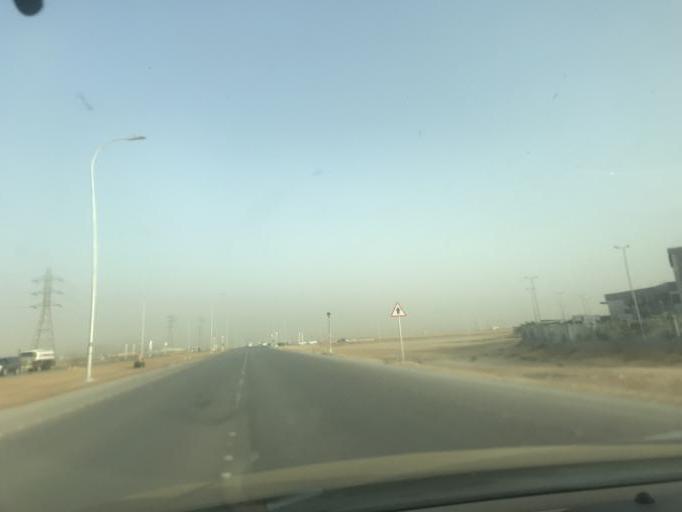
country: SA
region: Ar Riyad
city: Riyadh
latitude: 24.9165
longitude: 46.6976
